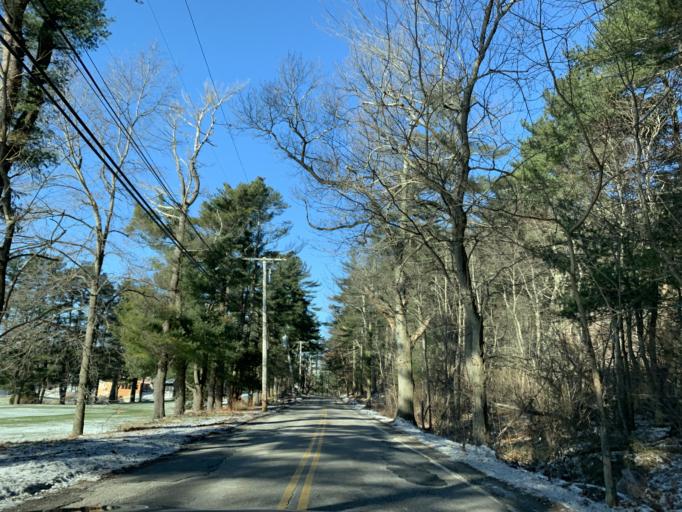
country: US
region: Massachusetts
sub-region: Norfolk County
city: Canton
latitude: 42.1995
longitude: -71.1274
